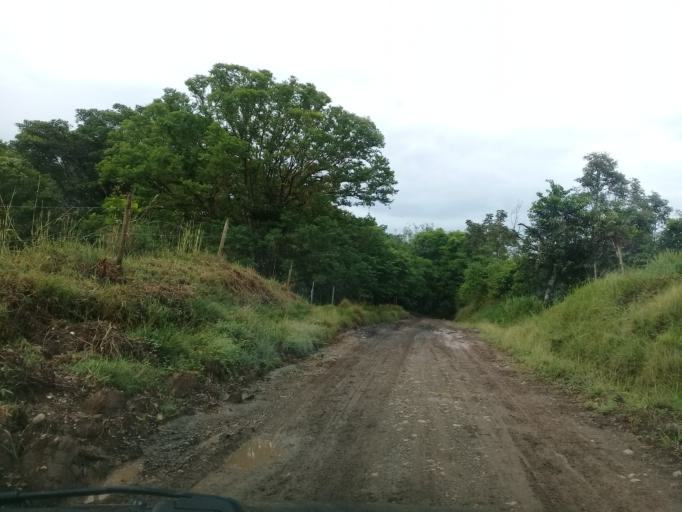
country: CO
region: Cundinamarca
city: Yacopi
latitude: 5.6992
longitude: -74.4436
